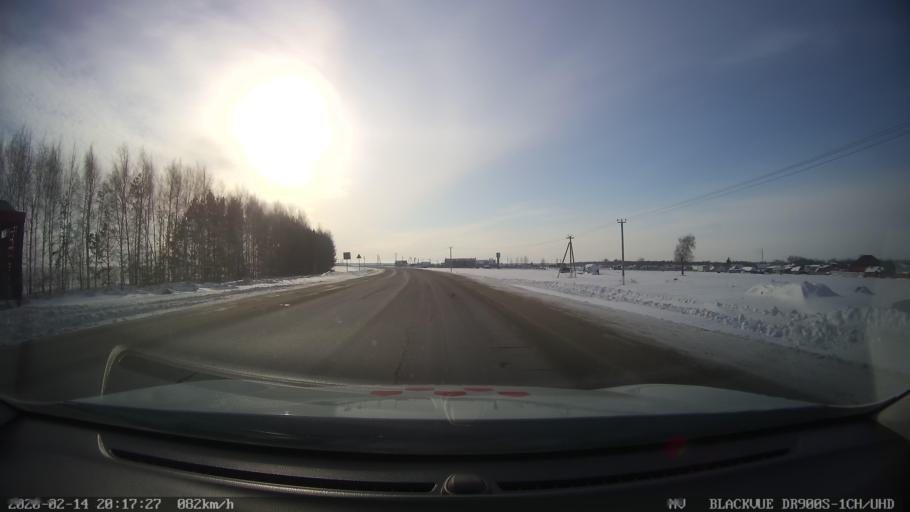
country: RU
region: Tatarstan
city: Verkhniy Uslon
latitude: 55.5998
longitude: 48.8775
